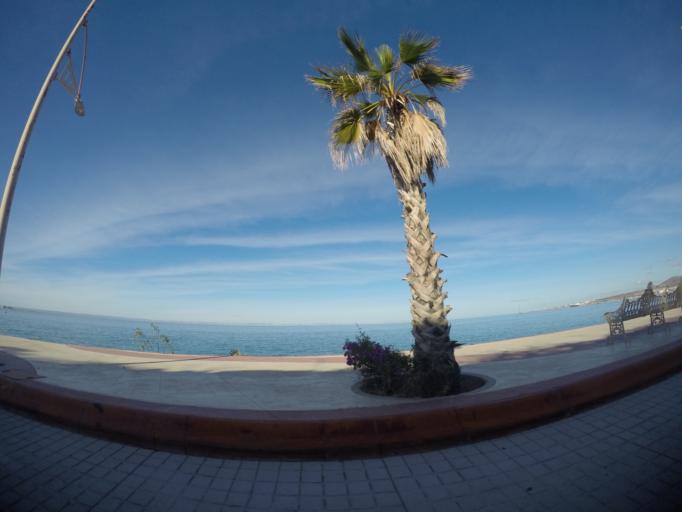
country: MX
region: Baja California Sur
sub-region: La Paz
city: La Paz
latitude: 24.1908
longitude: -110.2949
